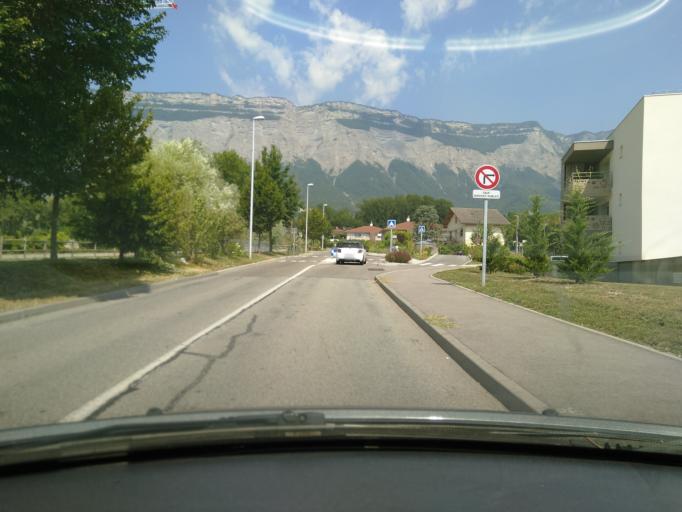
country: FR
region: Rhone-Alpes
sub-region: Departement de l'Isere
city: Montbonnot-Saint-Martin
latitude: 45.2241
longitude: 5.8136
